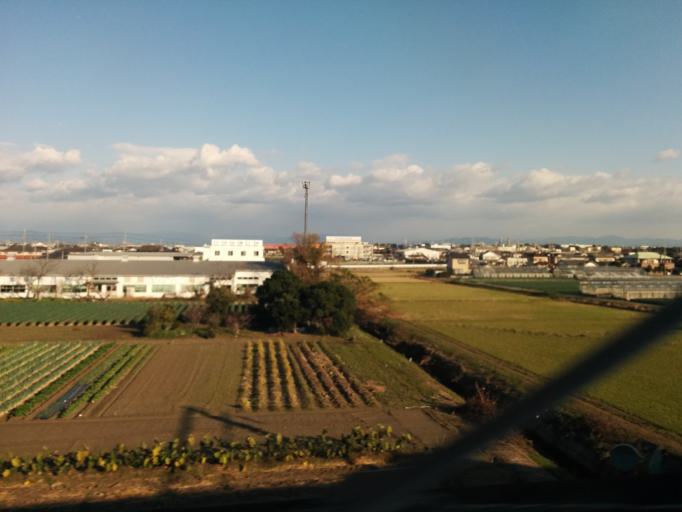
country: JP
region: Shizuoka
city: Iwata
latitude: 34.7031
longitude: 137.8319
